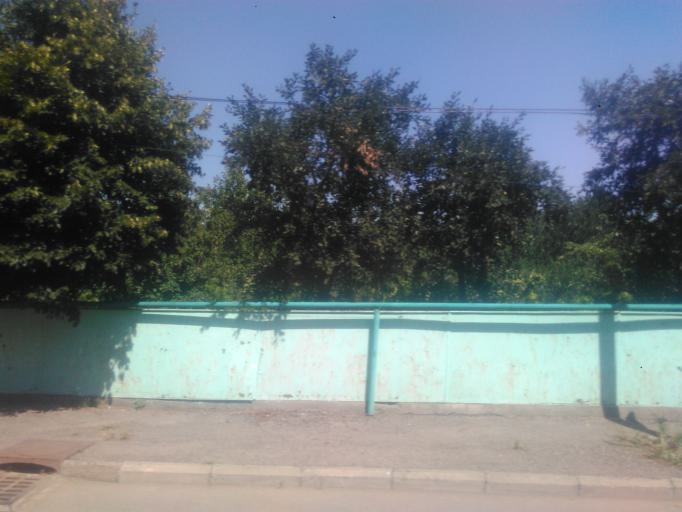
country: GE
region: T'bilisi
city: Tbilisi
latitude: 41.7031
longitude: 44.8880
